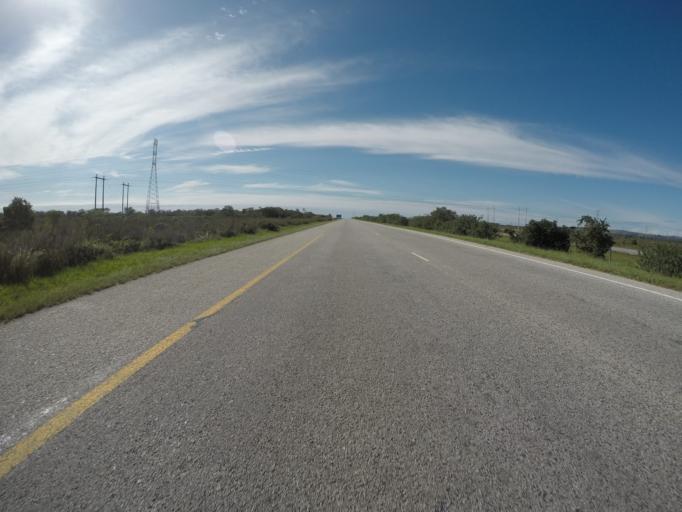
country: ZA
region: Eastern Cape
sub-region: Nelson Mandela Bay Metropolitan Municipality
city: Port Elizabeth
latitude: -33.9487
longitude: 25.4463
